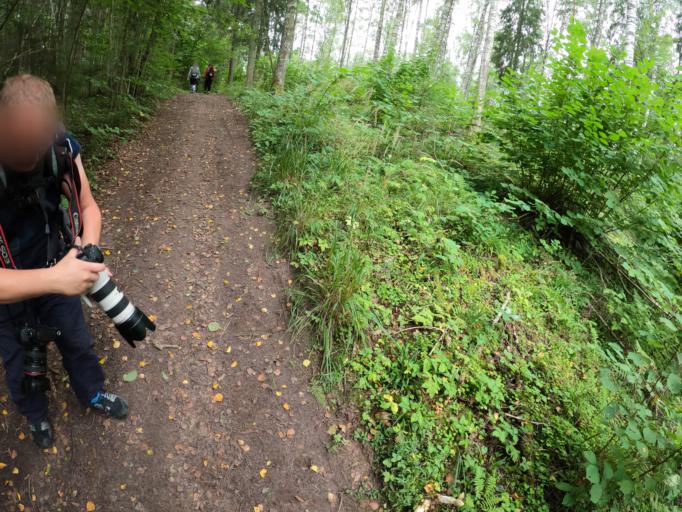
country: LV
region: Tukuma Rajons
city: Tukums
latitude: 57.0008
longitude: 23.1272
